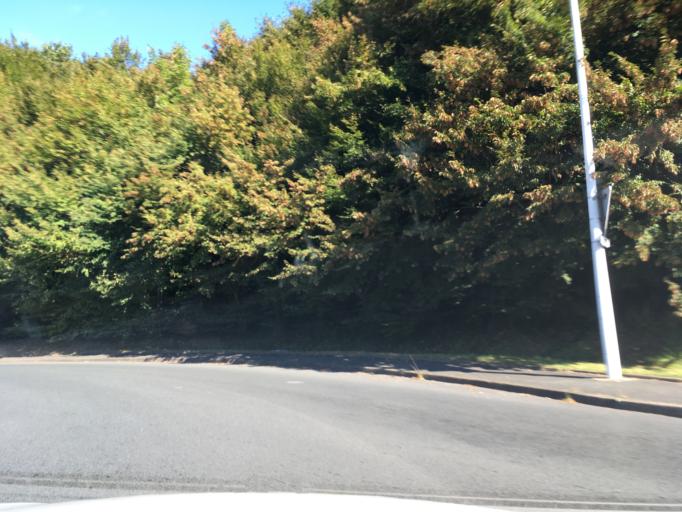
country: FR
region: Aquitaine
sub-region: Departement des Pyrenees-Atlantiques
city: Bayonne
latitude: 43.5022
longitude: -1.4784
